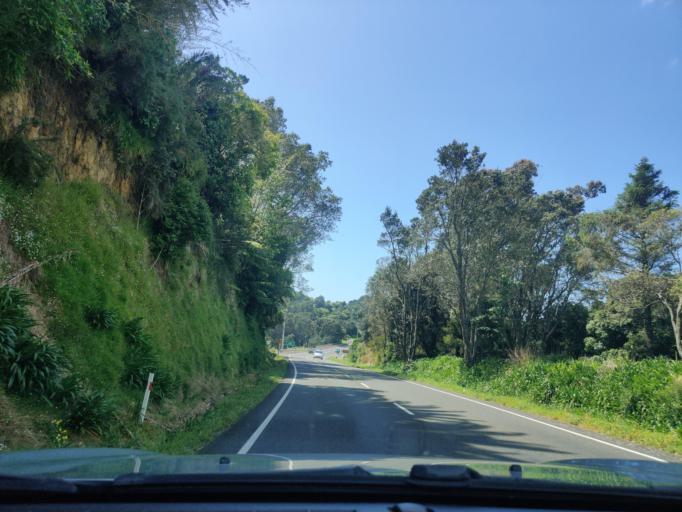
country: NZ
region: Taranaki
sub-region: New Plymouth District
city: New Plymouth
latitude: -39.1141
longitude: 173.9581
